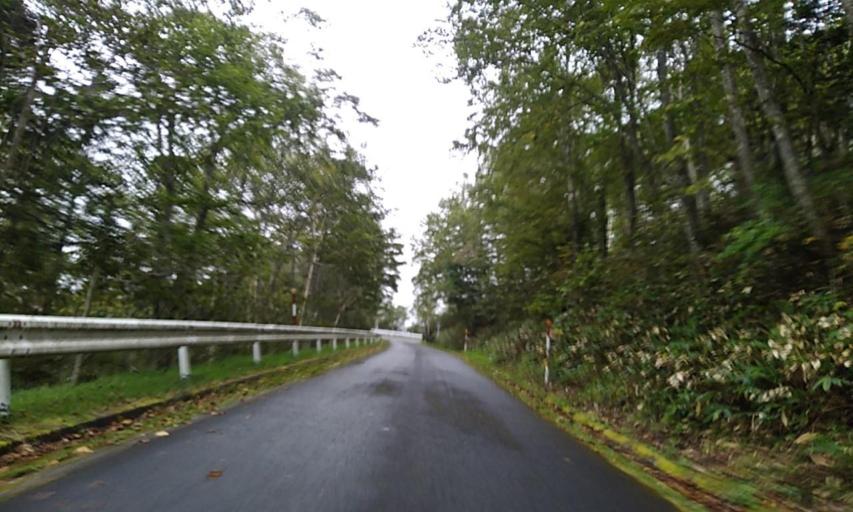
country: JP
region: Hokkaido
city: Bihoro
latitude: 43.5789
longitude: 144.2348
